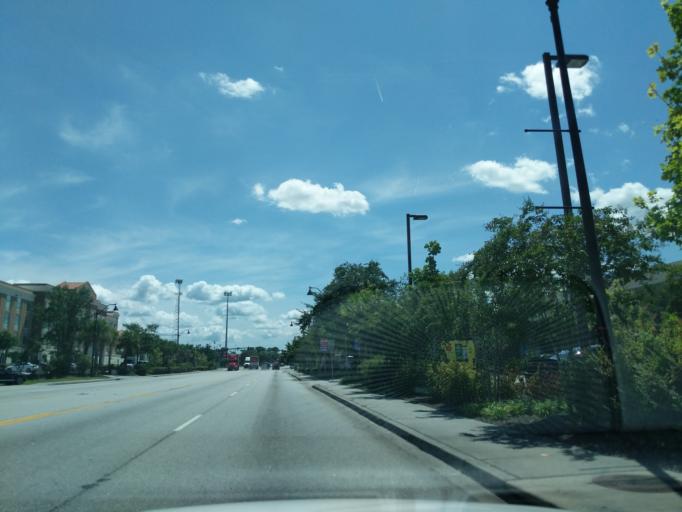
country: US
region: South Carolina
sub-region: Charleston County
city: North Charleston
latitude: 32.8677
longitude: -80.0131
